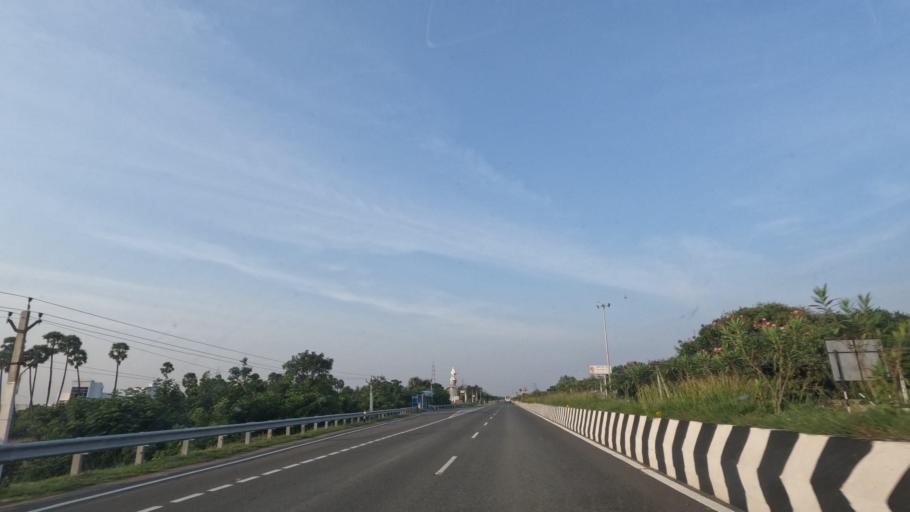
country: IN
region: Tamil Nadu
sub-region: Kancheepuram
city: Mamallapuram
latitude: 12.6975
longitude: 80.2207
